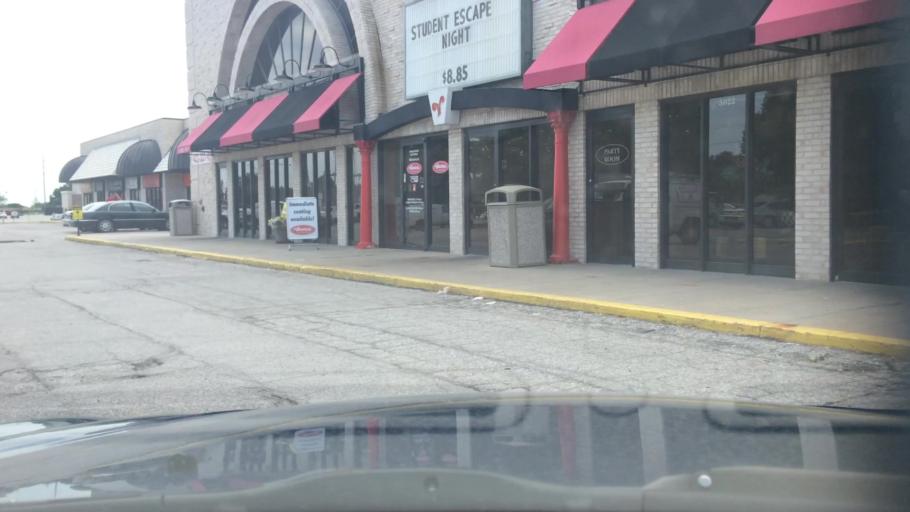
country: US
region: Nebraska
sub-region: Douglas County
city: Ralston
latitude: 41.2085
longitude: -96.0817
